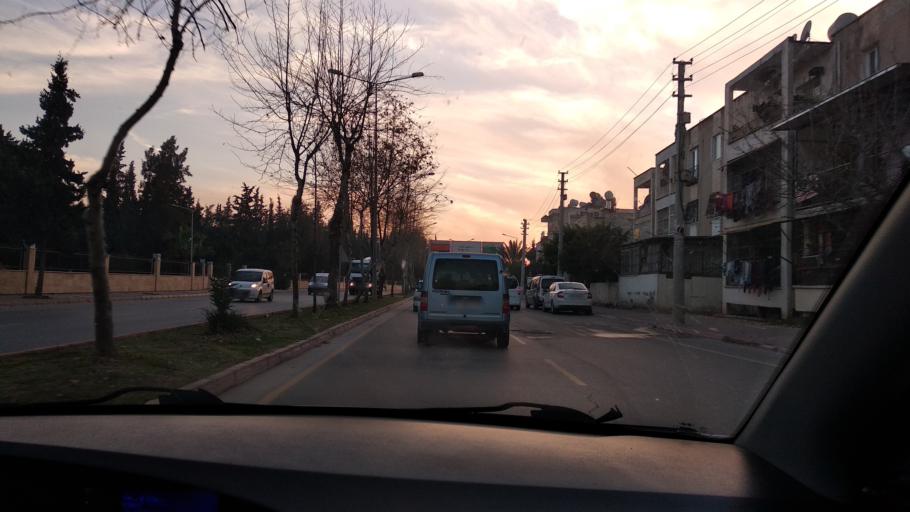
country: TR
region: Mersin
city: Mercin
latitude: 36.8224
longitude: 34.6005
